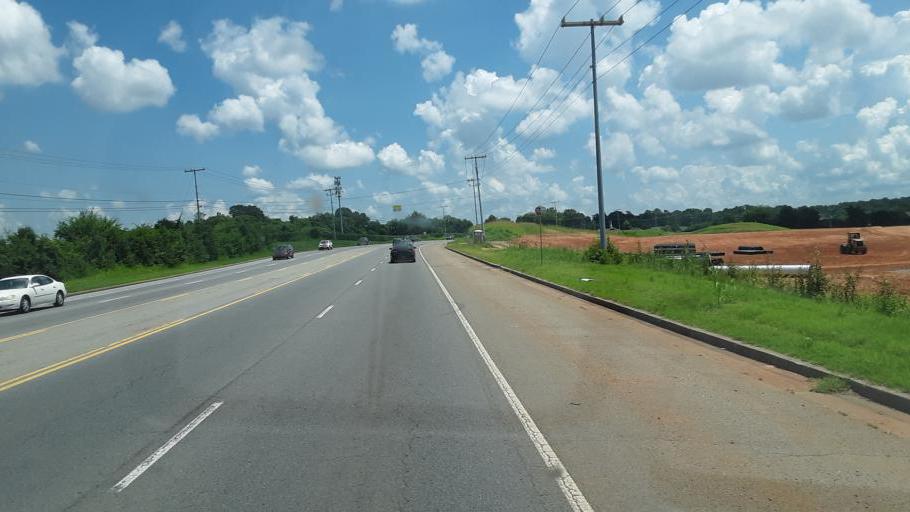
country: US
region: Kentucky
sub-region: Christian County
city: Oak Grove
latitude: 36.6309
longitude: -87.3875
